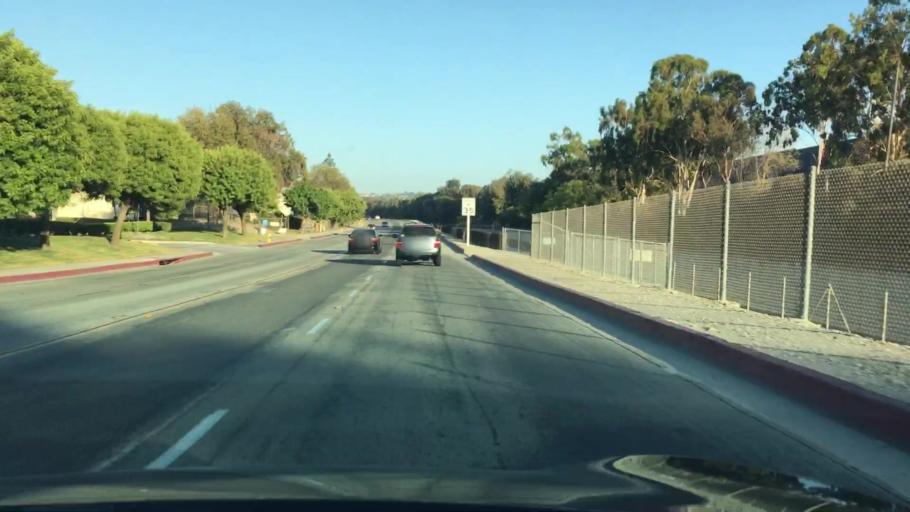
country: US
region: California
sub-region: Los Angeles County
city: South San Jose Hills
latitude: 34.0031
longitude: -117.9037
